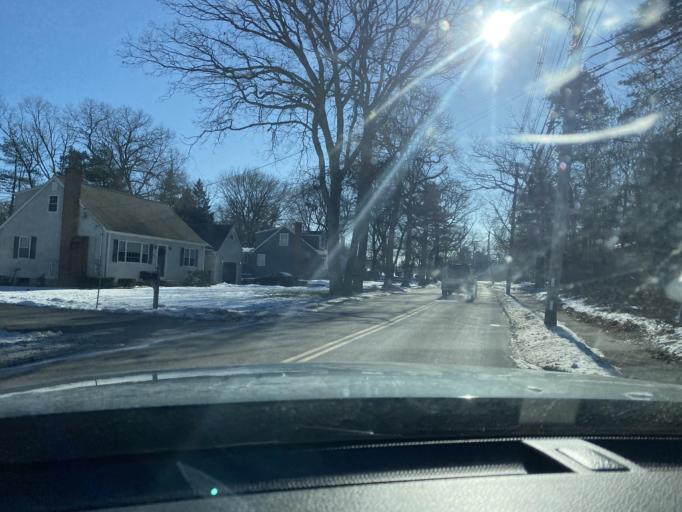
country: US
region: Massachusetts
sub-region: Norfolk County
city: Walpole
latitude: 42.1612
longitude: -71.2515
